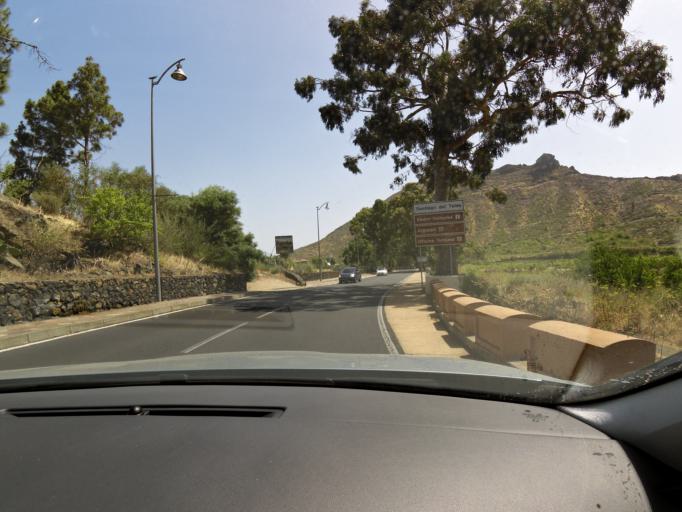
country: ES
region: Canary Islands
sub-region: Provincia de Santa Cruz de Tenerife
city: Santiago del Teide
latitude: 28.3003
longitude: -16.8148
